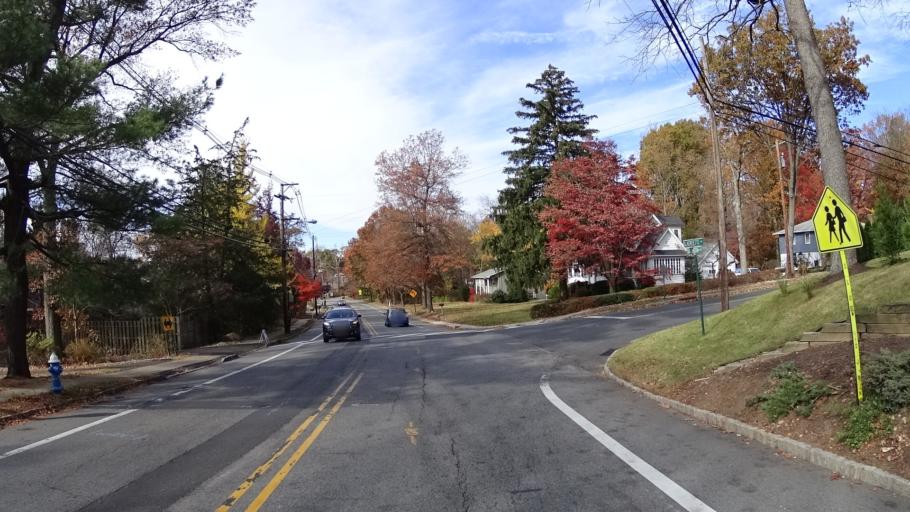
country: US
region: New Jersey
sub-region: Morris County
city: Chatham
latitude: 40.7273
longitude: -74.4095
